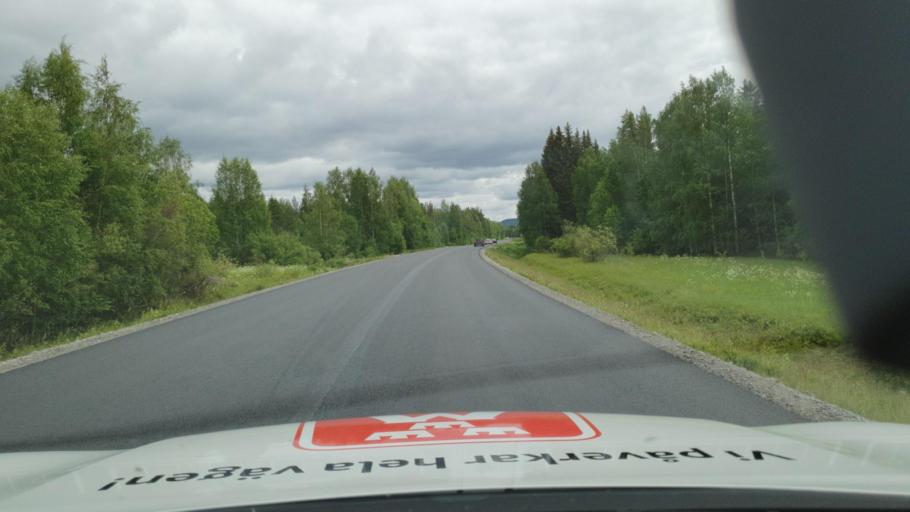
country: SE
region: Vaesterbotten
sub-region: Asele Kommun
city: Asele
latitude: 64.1692
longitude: 17.3142
